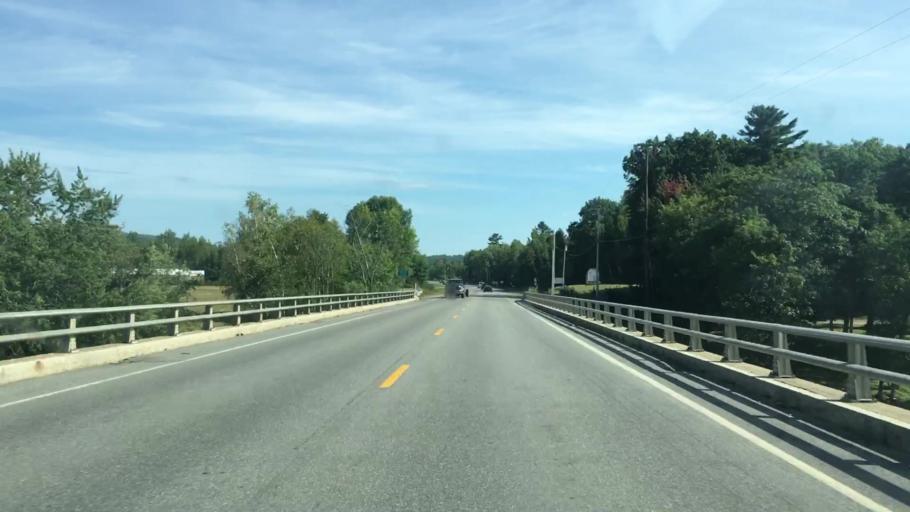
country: US
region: Maine
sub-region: Penobscot County
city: Lincoln
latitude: 45.3619
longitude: -68.5470
